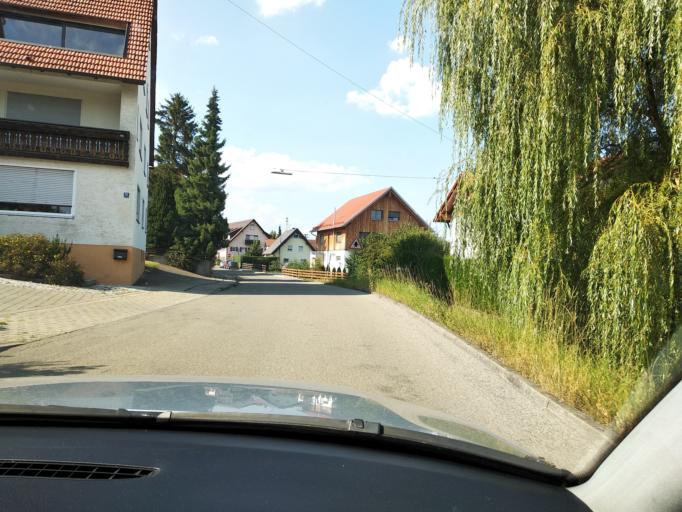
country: DE
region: Bavaria
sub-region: Swabia
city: Memmingen
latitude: 48.0024
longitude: 10.1822
